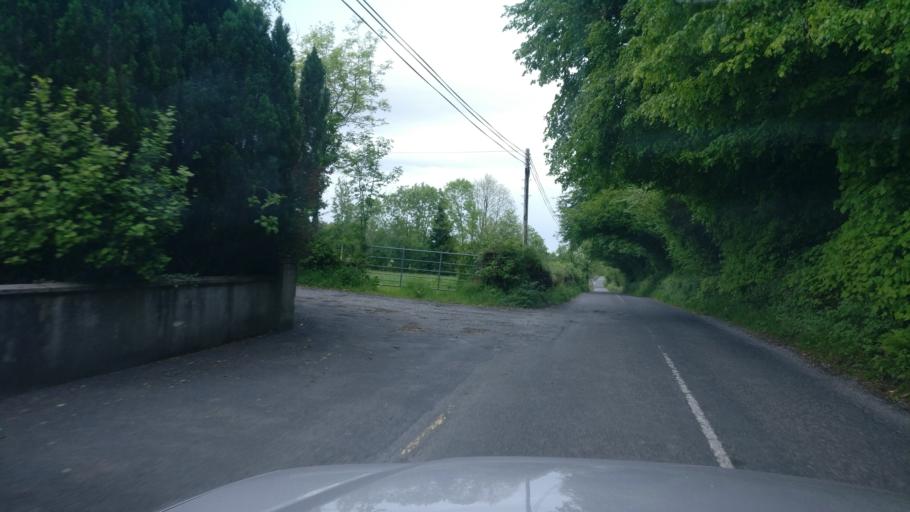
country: IE
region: Connaught
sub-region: County Galway
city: Loughrea
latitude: 53.0895
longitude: -8.4806
